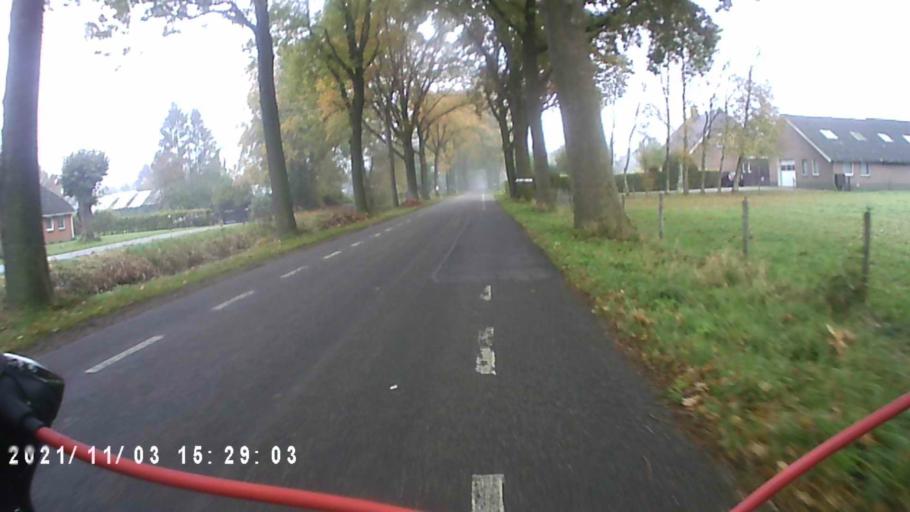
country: NL
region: Groningen
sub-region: Gemeente Leek
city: Leek
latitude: 53.1372
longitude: 6.3736
